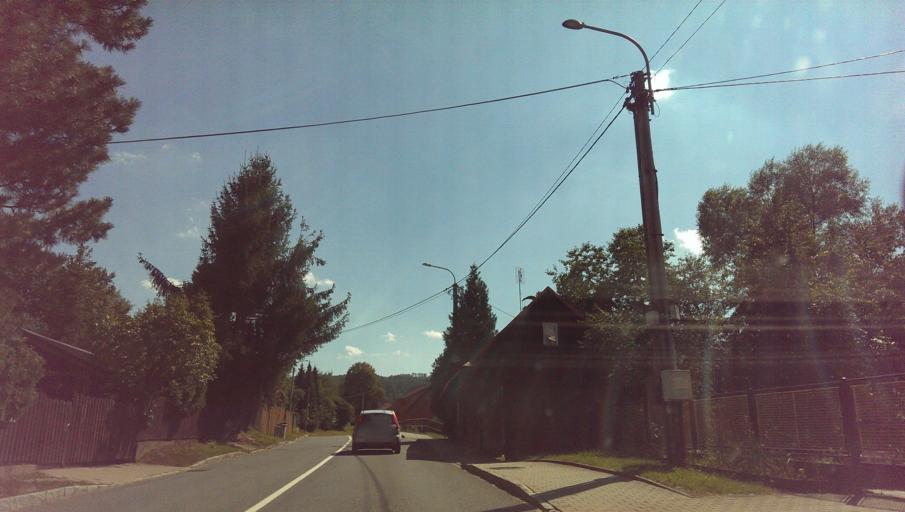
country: CZ
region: Zlin
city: Lesna
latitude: 49.4583
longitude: 17.8926
